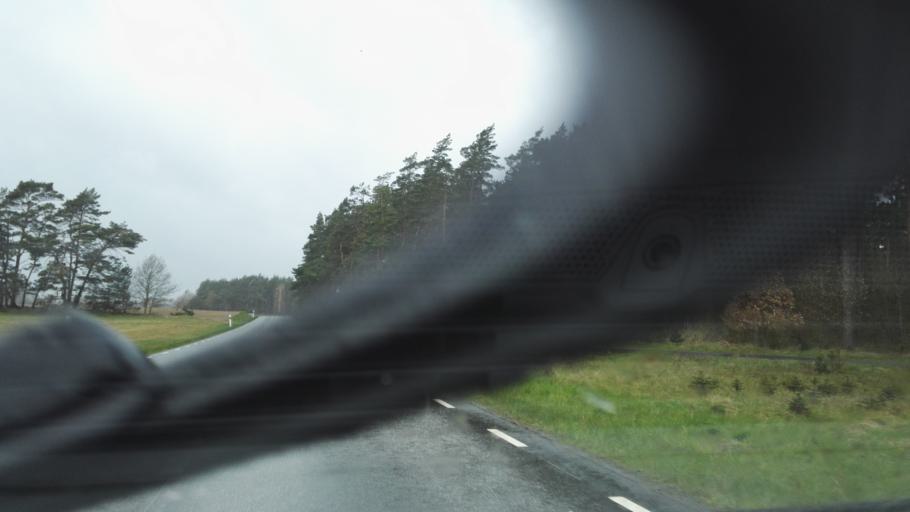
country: SE
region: Skane
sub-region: Simrishamns Kommun
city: Kivik
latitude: 55.7122
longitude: 14.1632
